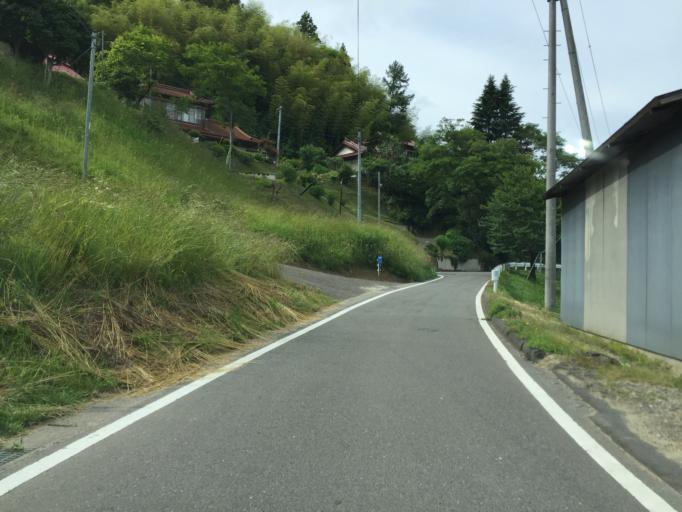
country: JP
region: Fukushima
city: Funehikimachi-funehiki
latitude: 37.4521
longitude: 140.6400
